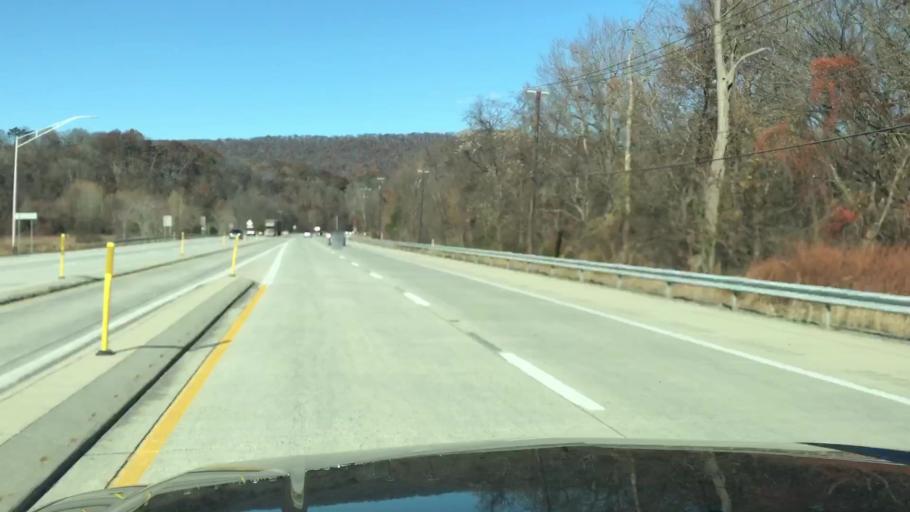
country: US
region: Pennsylvania
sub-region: Dauphin County
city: Millersburg
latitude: 40.5049
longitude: -76.9785
